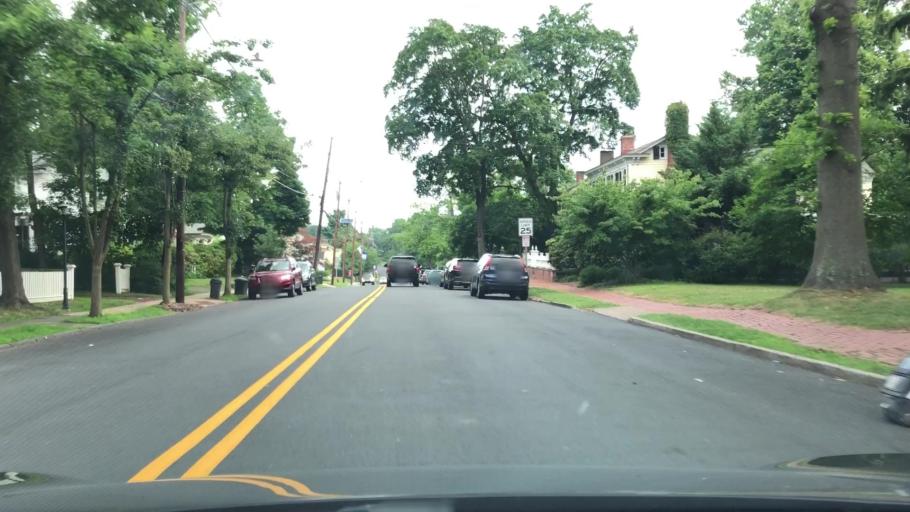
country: US
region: New Jersey
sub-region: Mercer County
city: Pennington
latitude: 40.3291
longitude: -74.7912
